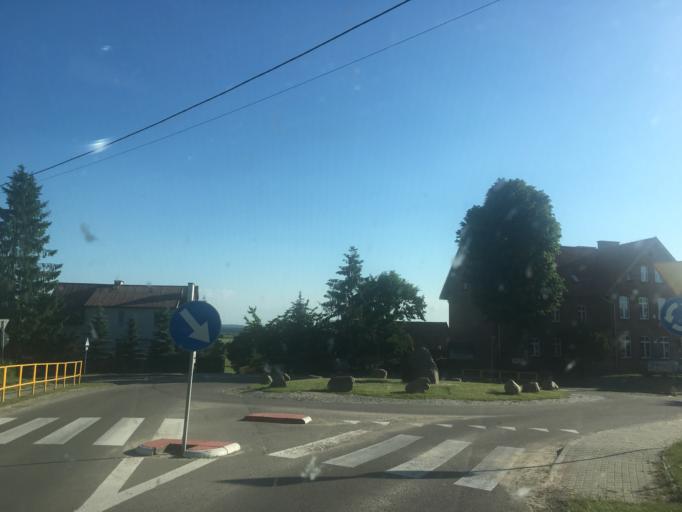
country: PL
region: Warmian-Masurian Voivodeship
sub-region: Powiat ostrodzki
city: Ostroda
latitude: 53.6768
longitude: 20.0489
